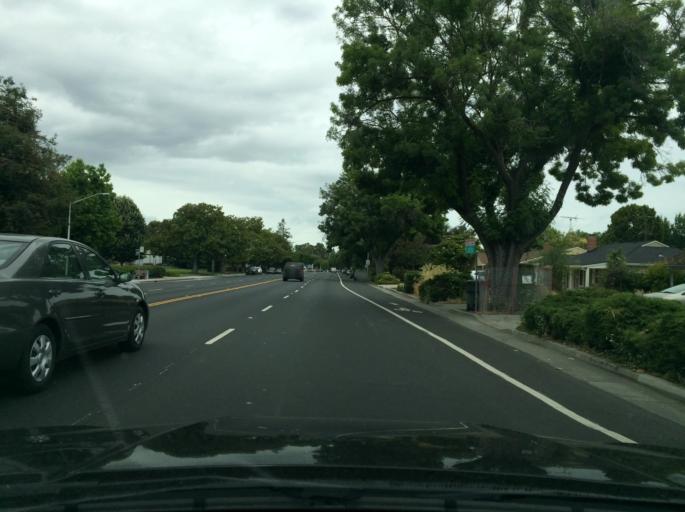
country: US
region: California
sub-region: Santa Clara County
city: Los Altos
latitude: 37.4176
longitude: -122.1059
